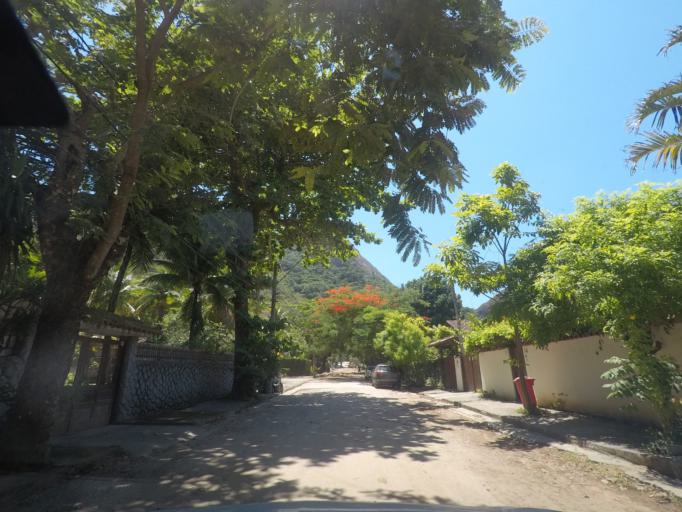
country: BR
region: Rio de Janeiro
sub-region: Niteroi
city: Niteroi
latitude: -22.9715
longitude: -43.0309
